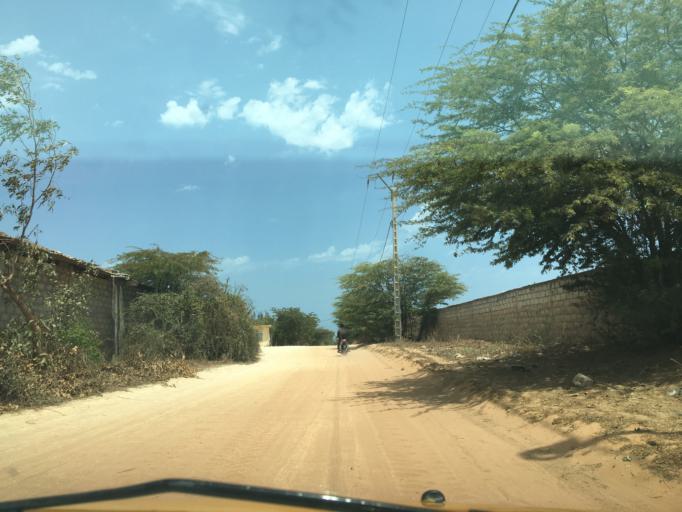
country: SN
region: Thies
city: Thies
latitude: 14.8206
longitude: -17.2012
